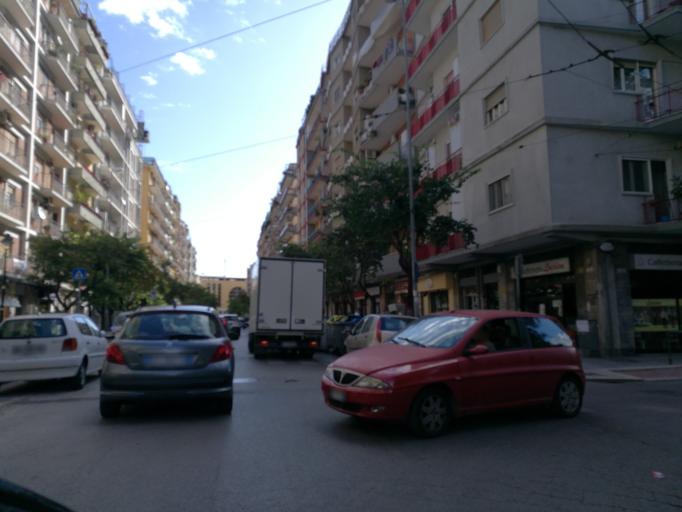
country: IT
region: Apulia
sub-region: Provincia di Bari
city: Bari
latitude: 41.1252
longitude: 16.8559
